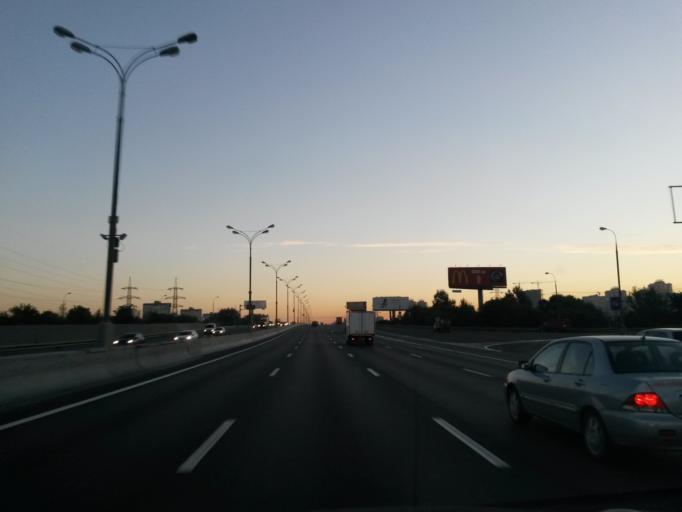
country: RU
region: Moskovskaya
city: Kuskovo
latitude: 55.7456
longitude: 37.8421
